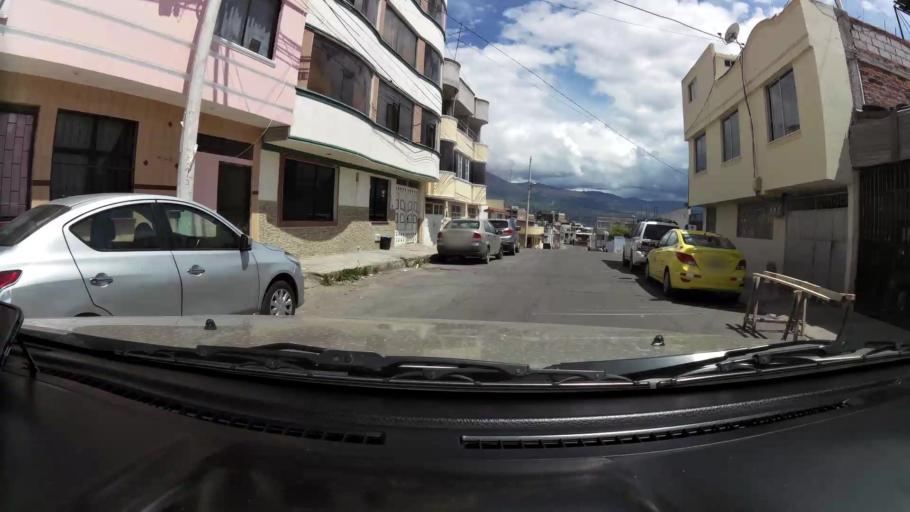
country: EC
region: Chimborazo
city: Riobamba
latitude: -1.6585
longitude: -78.6447
